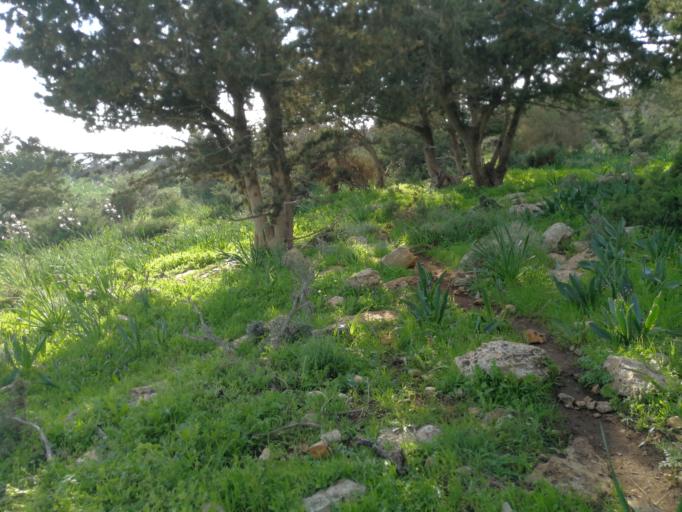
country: CY
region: Pafos
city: Pegeia
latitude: 34.9245
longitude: 32.3590
